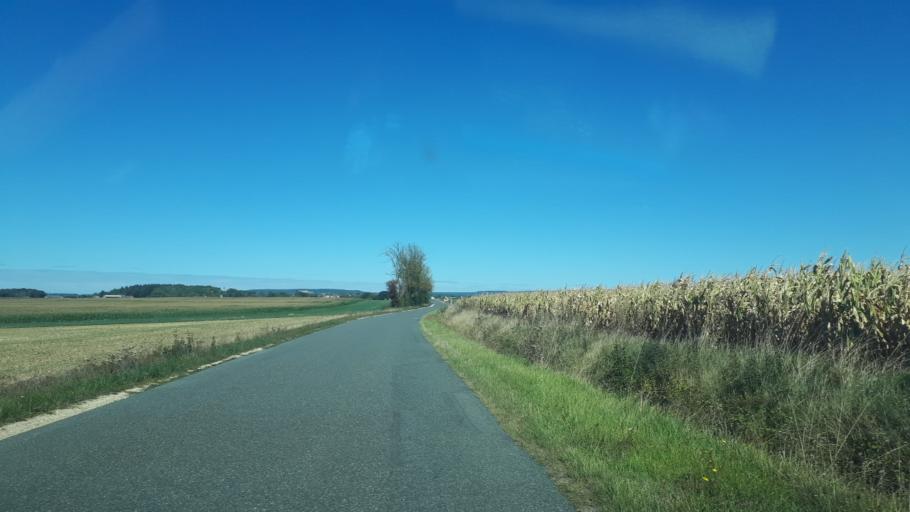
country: FR
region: Centre
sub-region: Departement du Cher
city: Sainte-Solange
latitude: 47.1713
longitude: 2.5686
